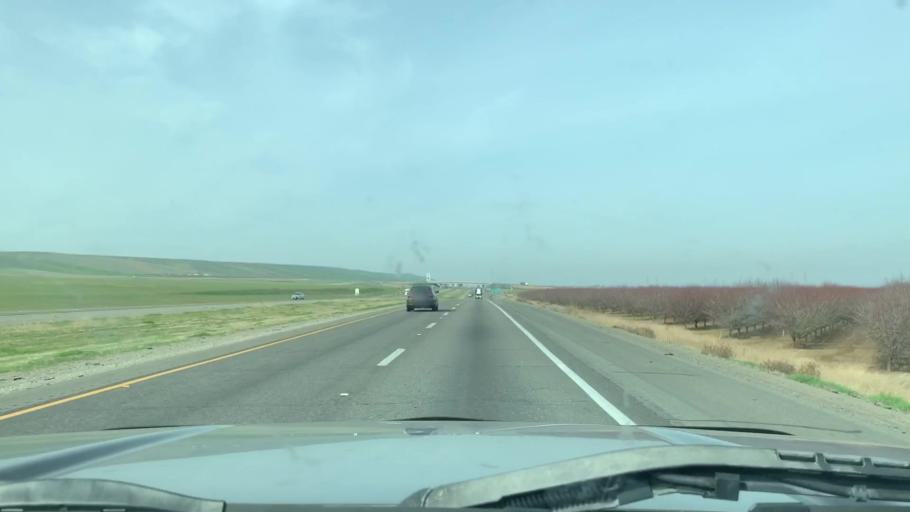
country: US
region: California
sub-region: Merced County
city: South Dos Palos
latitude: 36.8434
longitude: -120.7690
